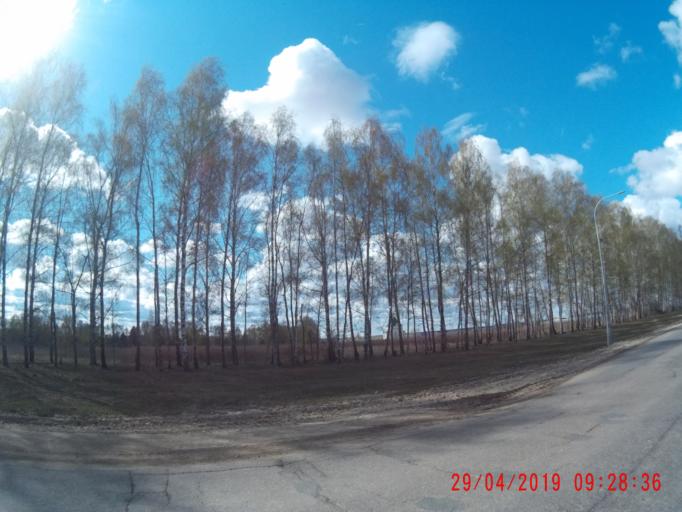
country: RU
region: Nizjnij Novgorod
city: Diveyevo
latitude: 55.0471
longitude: 43.2724
